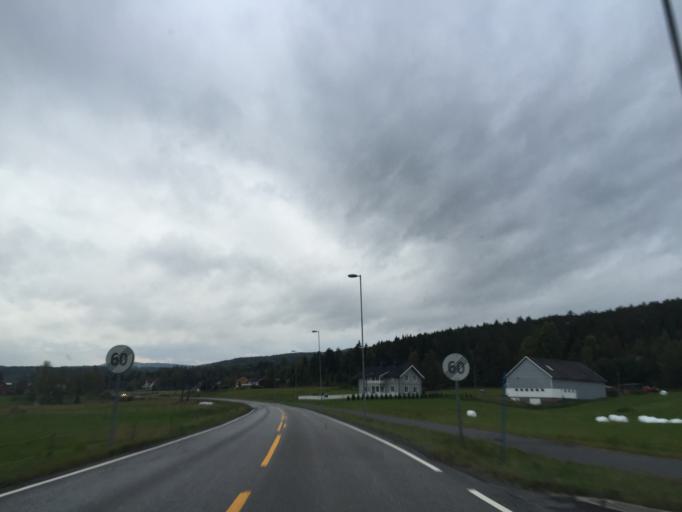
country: NO
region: Hedmark
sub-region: Nord-Odal
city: Sand
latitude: 60.3838
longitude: 11.5394
